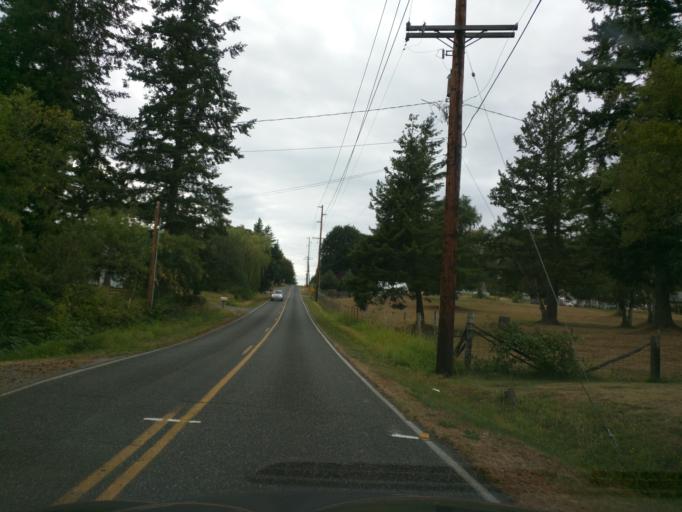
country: US
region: Washington
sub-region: Whatcom County
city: Bellingham
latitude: 48.8147
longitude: -122.4561
